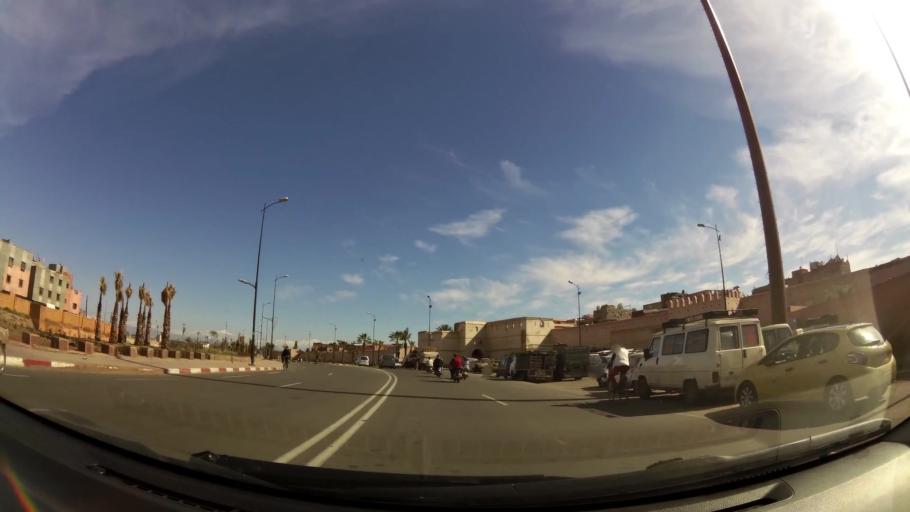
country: MA
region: Marrakech-Tensift-Al Haouz
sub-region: Marrakech
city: Marrakesh
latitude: 31.6348
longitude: -7.9784
